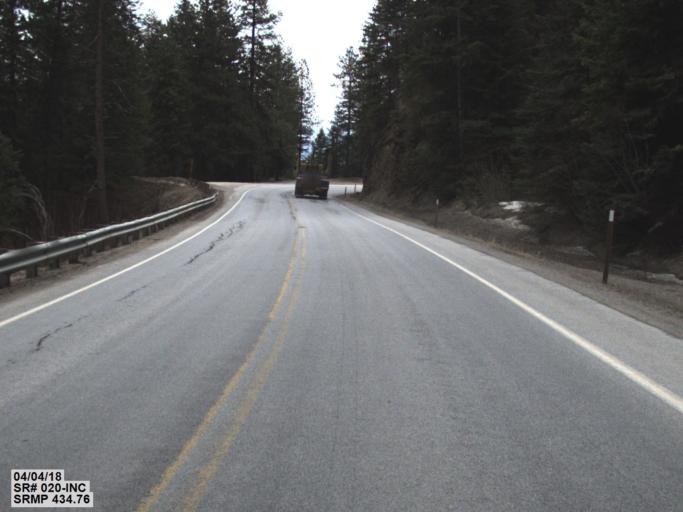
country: US
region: Washington
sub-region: Pend Oreille County
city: Newport
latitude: 48.2094
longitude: -117.0660
